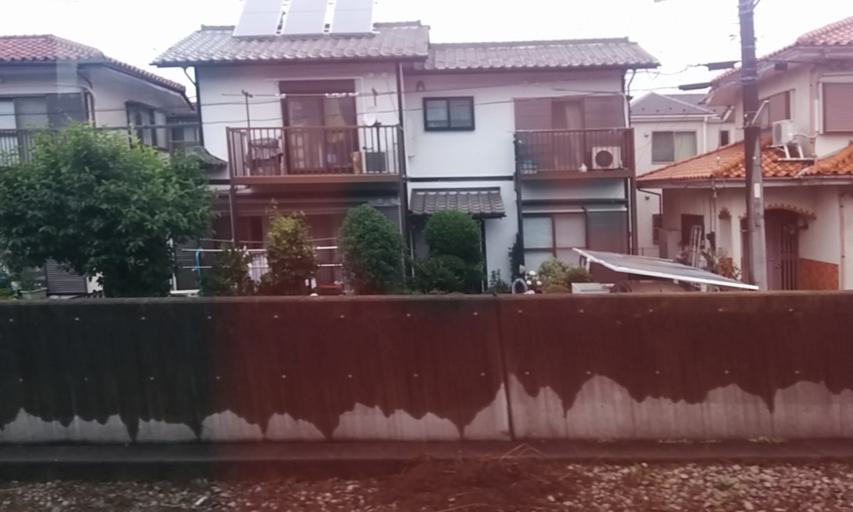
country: JP
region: Tokyo
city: Hino
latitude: 35.6427
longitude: 139.3721
